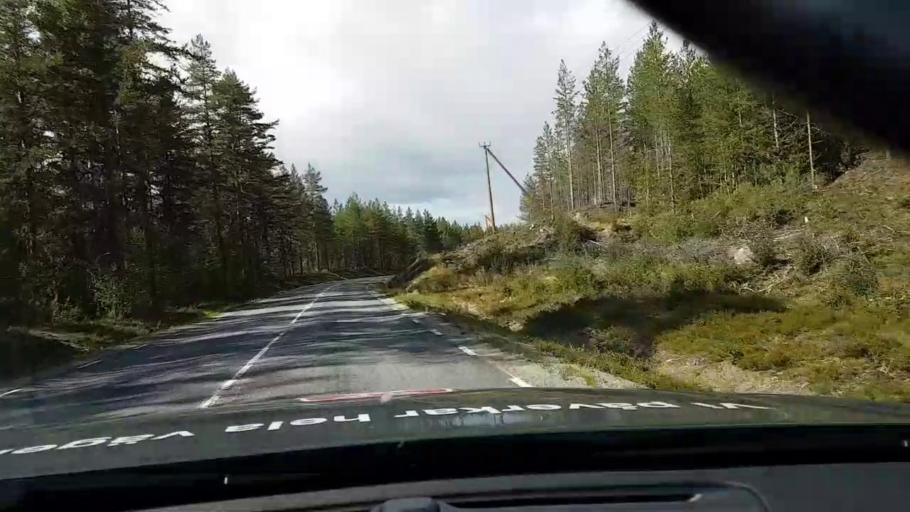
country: SE
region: Vaesterbotten
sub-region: Asele Kommun
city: Asele
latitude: 63.8502
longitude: 17.3970
